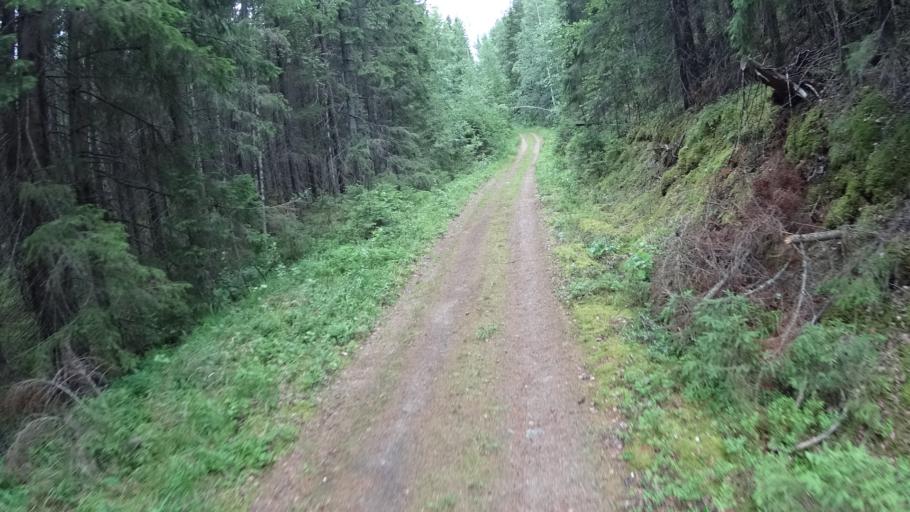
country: FI
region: Southern Savonia
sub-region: Mikkeli
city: Maentyharju
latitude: 61.1852
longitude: 26.8292
